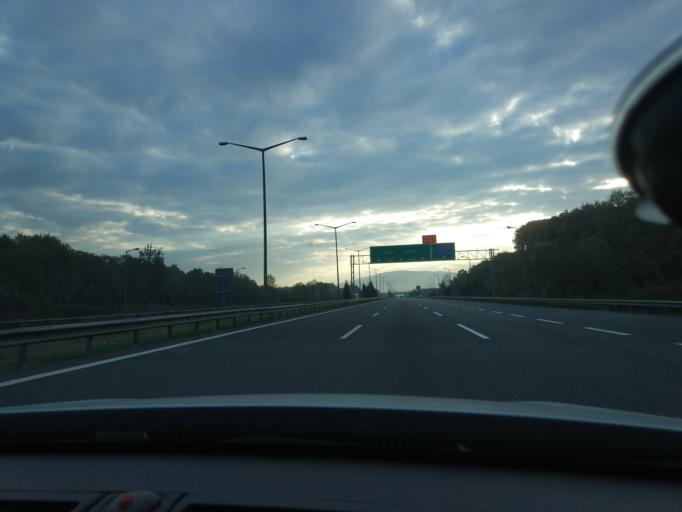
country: TR
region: Sakarya
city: Hendek
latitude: 40.7532
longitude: 30.7080
